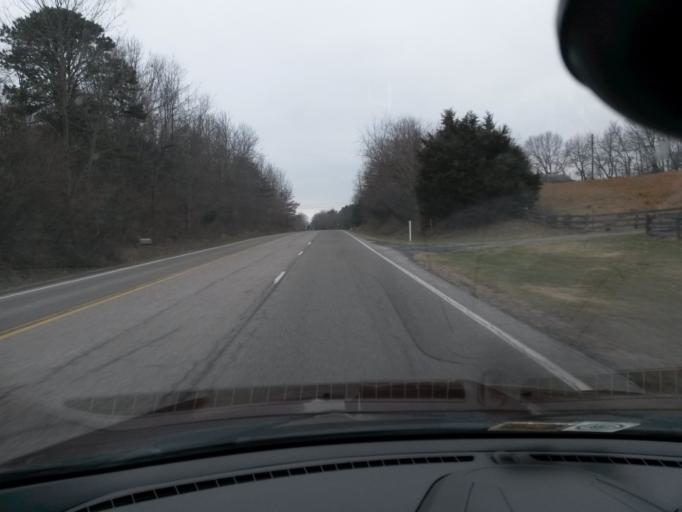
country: US
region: Virginia
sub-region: Augusta County
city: Stuarts Draft
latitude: 37.9567
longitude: -79.1819
